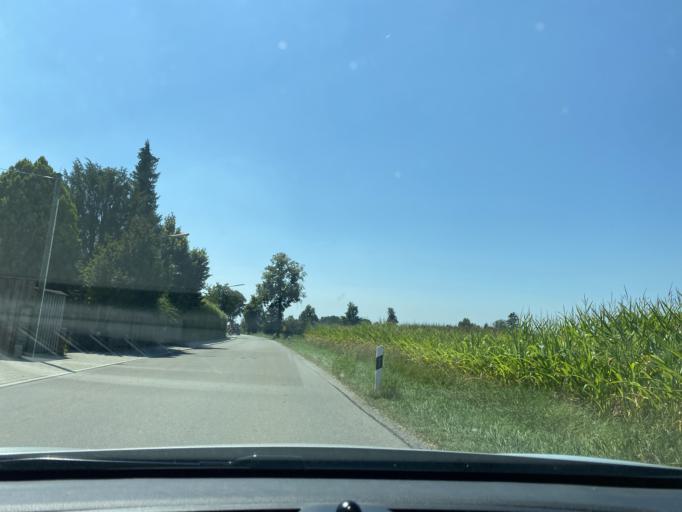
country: DE
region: Bavaria
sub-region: Upper Bavaria
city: Moosinning
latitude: 48.2704
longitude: 11.8455
